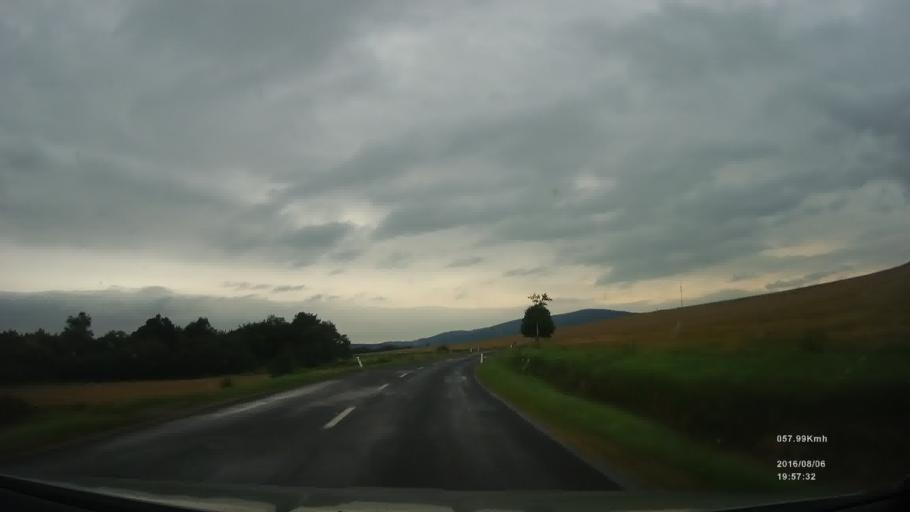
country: SK
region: Presovsky
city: Svidnik
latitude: 49.2756
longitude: 21.5760
